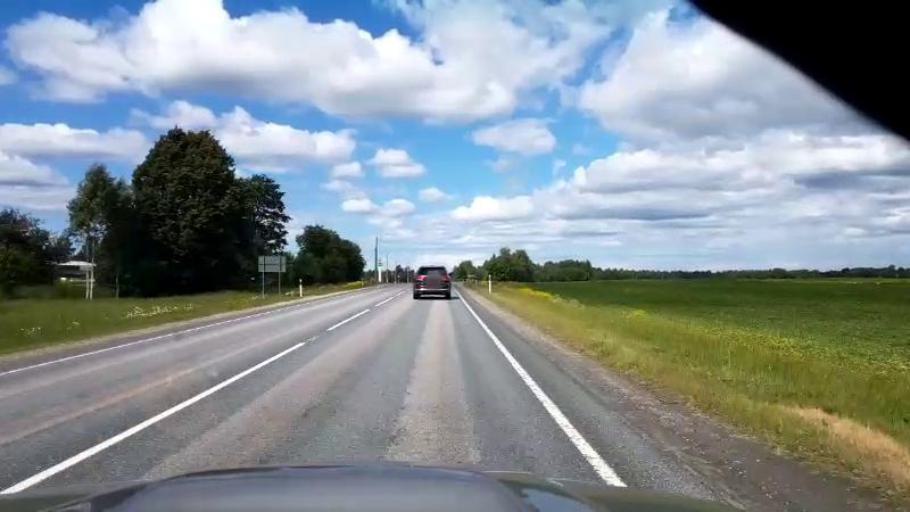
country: EE
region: Harju
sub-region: Saue linn
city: Saue
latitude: 59.1540
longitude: 24.5052
